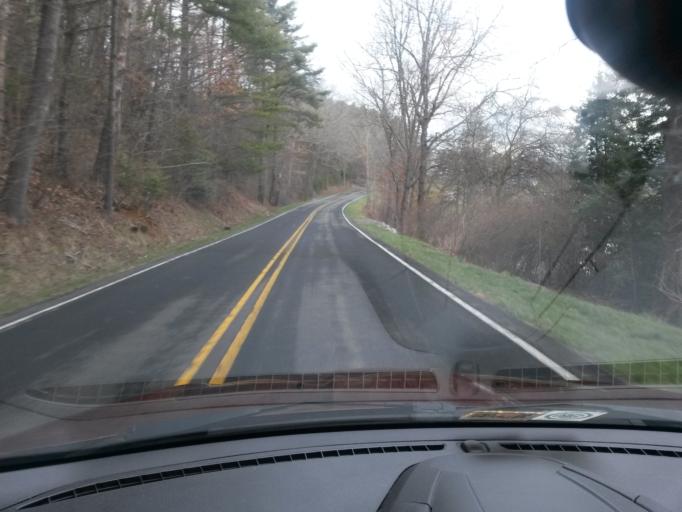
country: US
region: Virginia
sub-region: Bath County
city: Warm Springs
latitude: 38.2016
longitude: -79.7278
